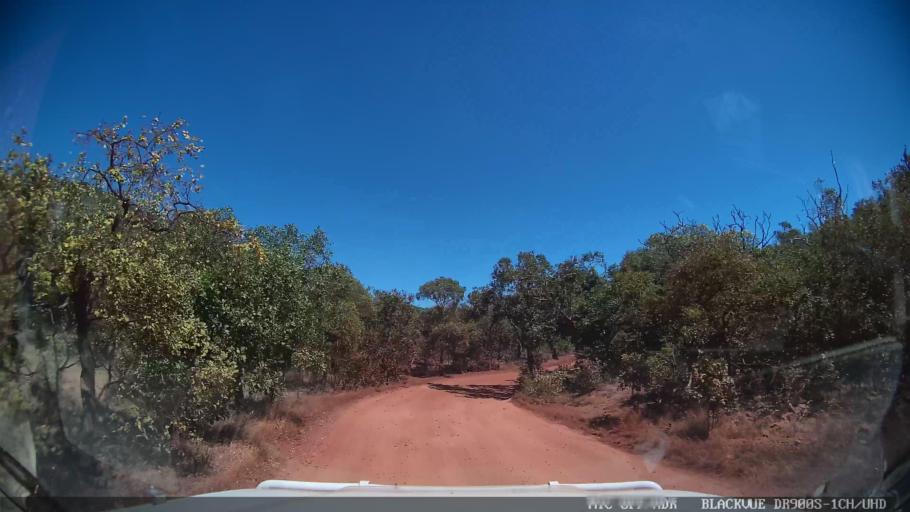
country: AU
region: Queensland
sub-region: Torres
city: Thursday Island
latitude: -10.7065
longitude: 142.5302
